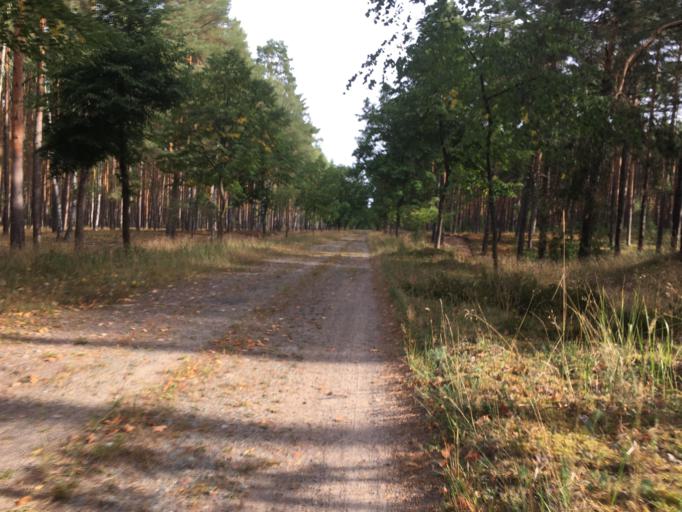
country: DE
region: Brandenburg
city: Marienwerder
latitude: 52.9528
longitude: 13.5246
